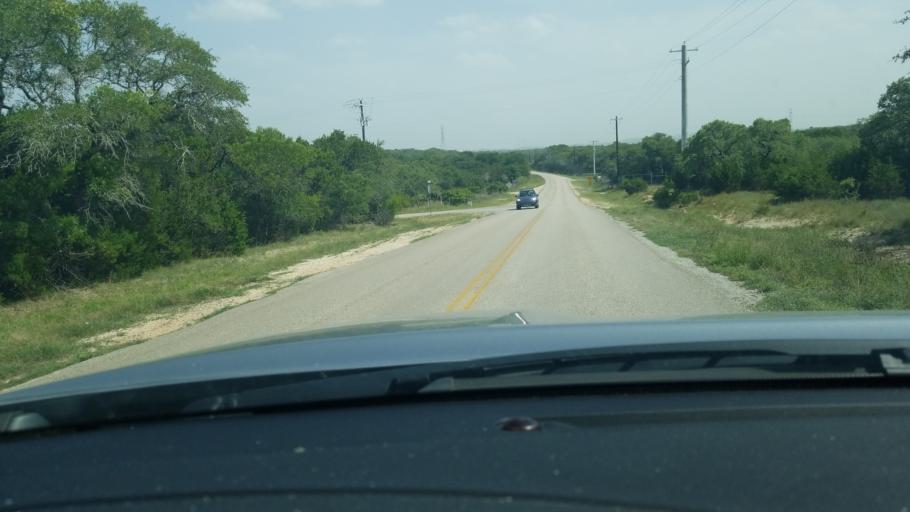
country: US
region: Texas
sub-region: Comal County
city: Bulverde
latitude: 29.7905
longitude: -98.4666
